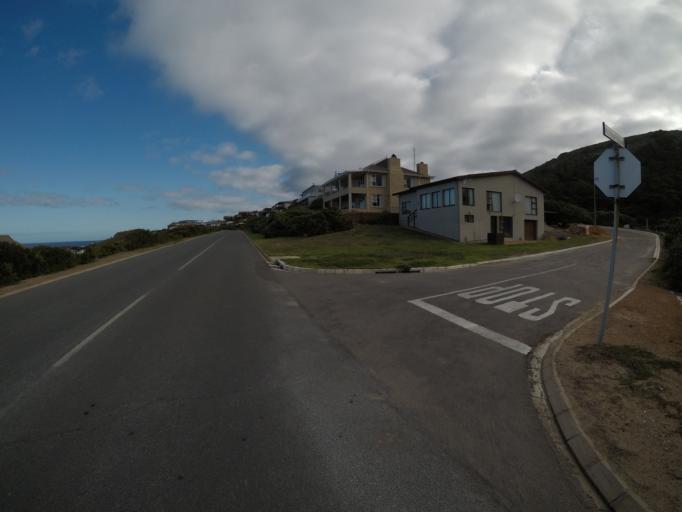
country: ZA
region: Western Cape
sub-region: Eden District Municipality
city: Riversdale
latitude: -34.4282
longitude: 21.3354
